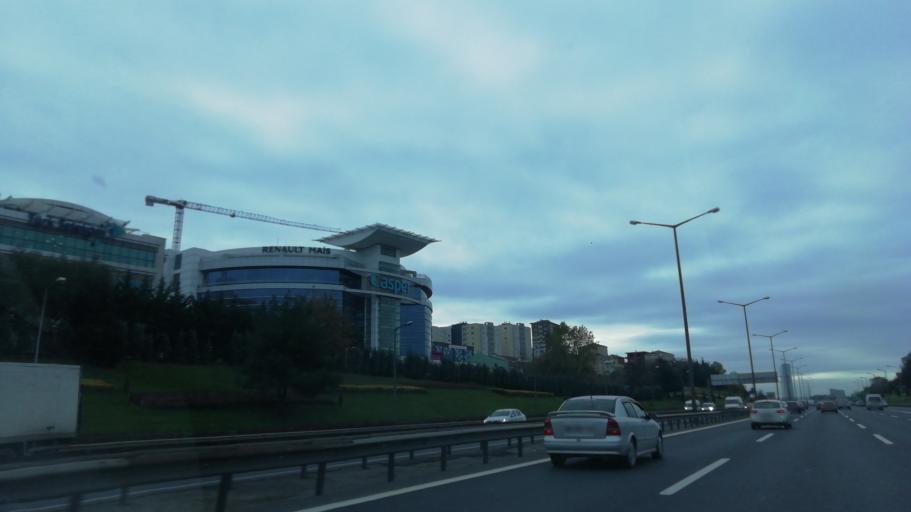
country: TR
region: Istanbul
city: Umraniye
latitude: 41.0273
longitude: 29.1208
